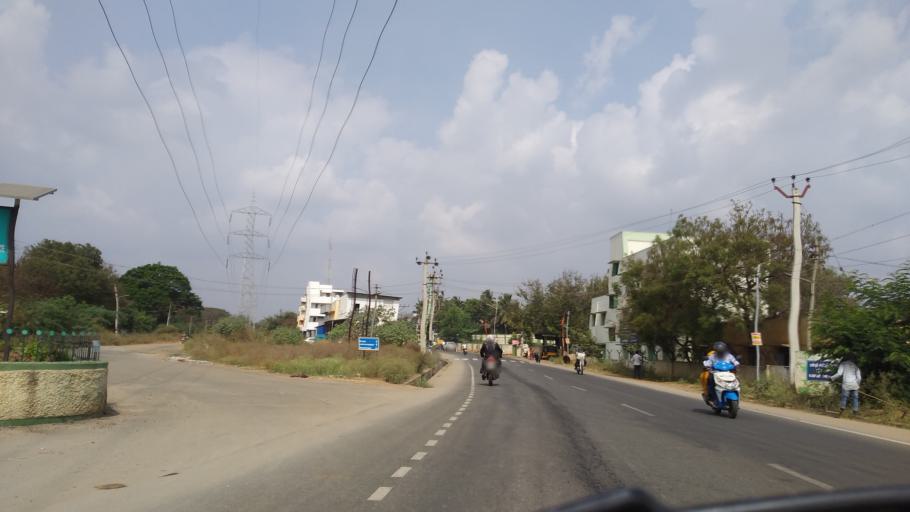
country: IN
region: Tamil Nadu
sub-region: Coimbatore
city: Perur
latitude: 10.9418
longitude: 76.9426
